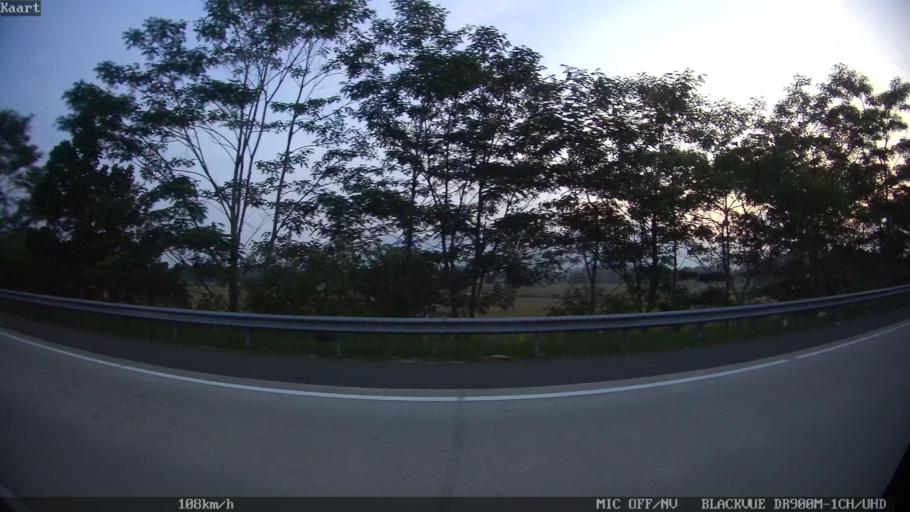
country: ID
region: Lampung
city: Pasuruan
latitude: -5.7423
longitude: 105.6949
